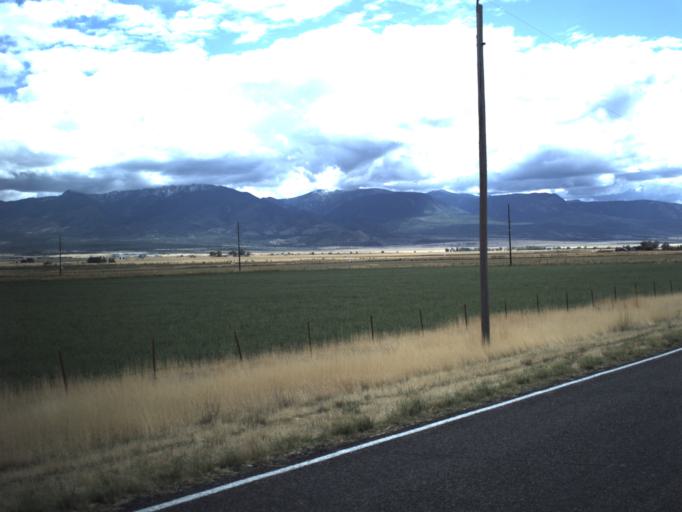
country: US
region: Utah
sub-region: Millard County
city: Fillmore
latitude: 38.9814
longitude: -112.4099
